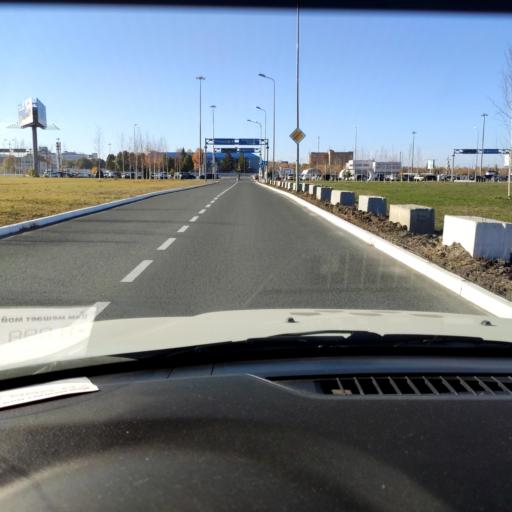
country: RU
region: Samara
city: Bereza
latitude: 53.5141
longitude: 50.1558
